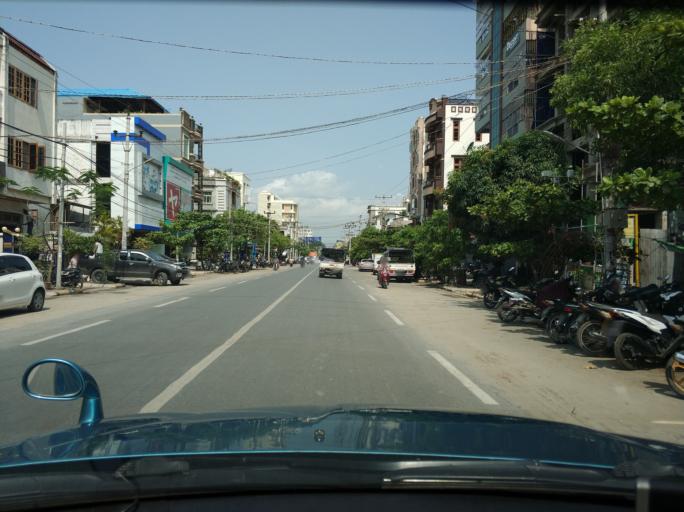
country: MM
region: Mandalay
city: Mandalay
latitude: 21.9660
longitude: 96.0891
